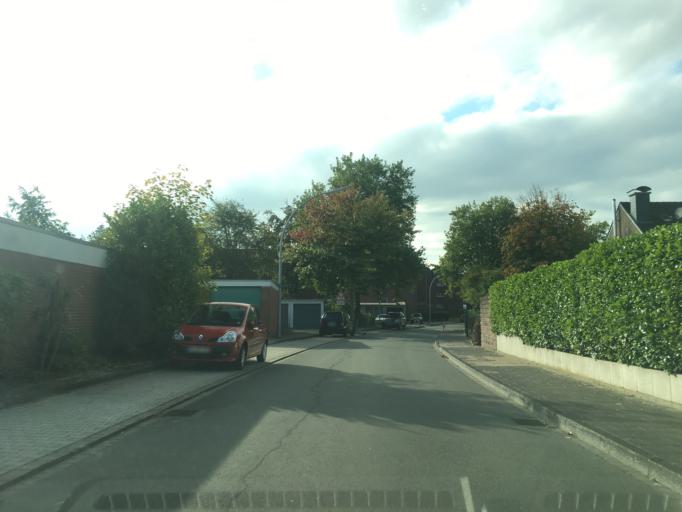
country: DE
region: North Rhine-Westphalia
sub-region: Regierungsbezirk Munster
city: Senden
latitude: 51.9257
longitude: 7.5258
